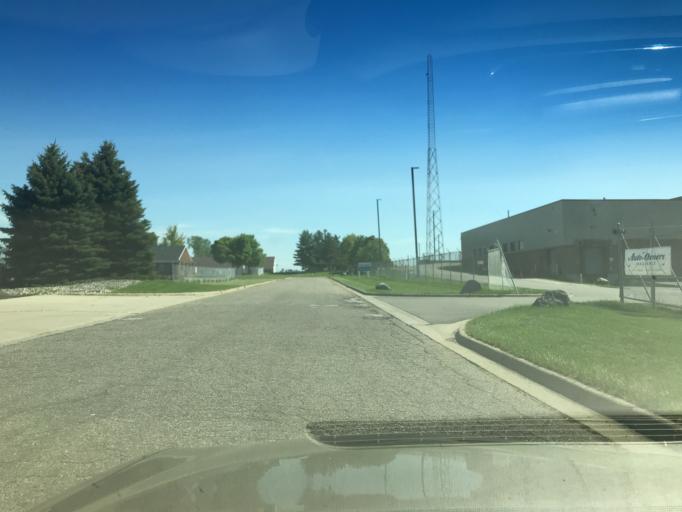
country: US
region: Michigan
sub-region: Eaton County
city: Waverly
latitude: 42.7036
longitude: -84.6675
